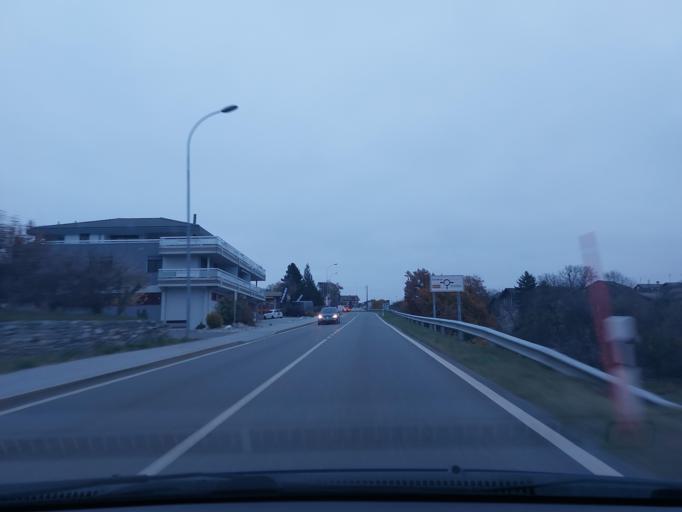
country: CH
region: Valais
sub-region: Sion District
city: Saviese
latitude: 46.2434
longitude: 7.3451
